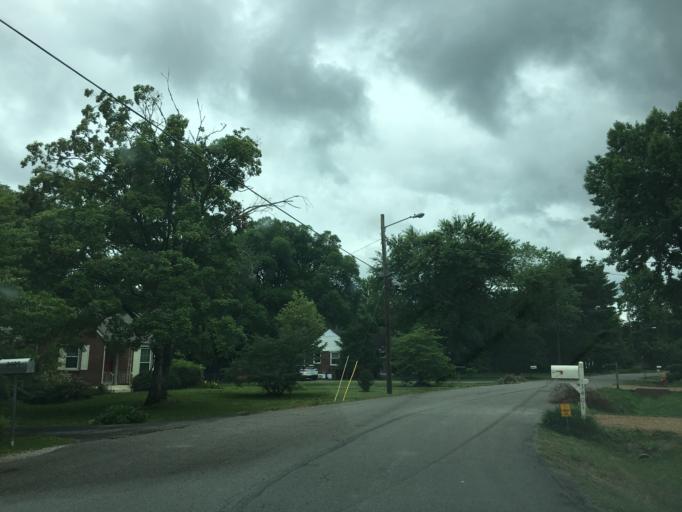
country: US
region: Tennessee
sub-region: Davidson County
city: Oak Hill
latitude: 36.1126
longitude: -86.7758
